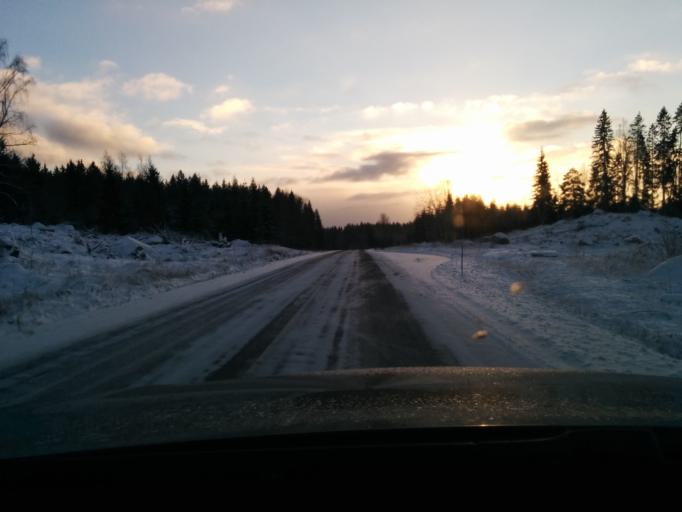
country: SE
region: Uppsala
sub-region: Tierps Kommun
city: Orbyhus
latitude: 60.2101
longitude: 17.6990
